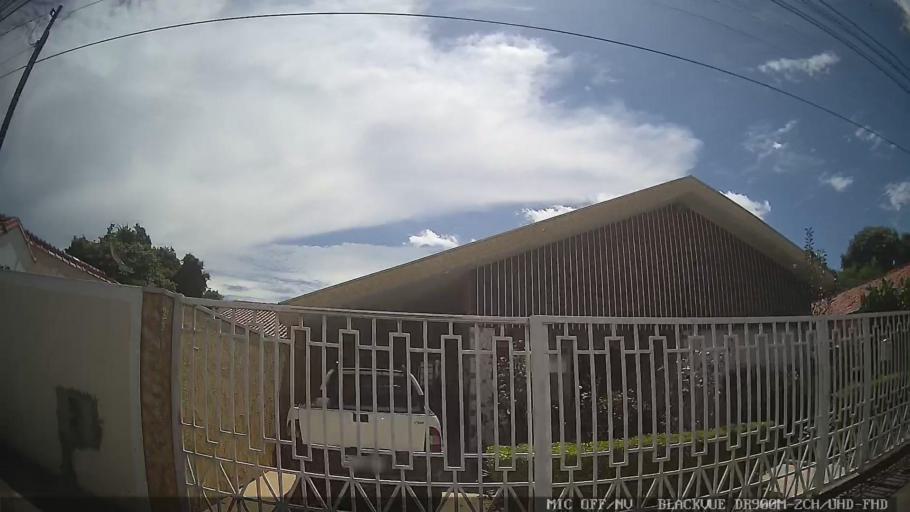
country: BR
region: Sao Paulo
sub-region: Conchas
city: Conchas
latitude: -23.0215
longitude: -48.0117
